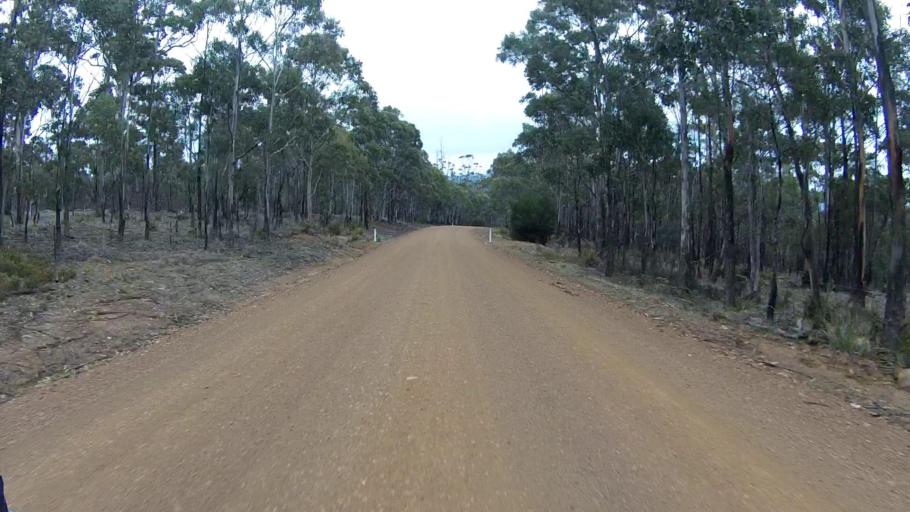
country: AU
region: Tasmania
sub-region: Sorell
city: Sorell
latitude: -42.5842
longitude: 147.8823
